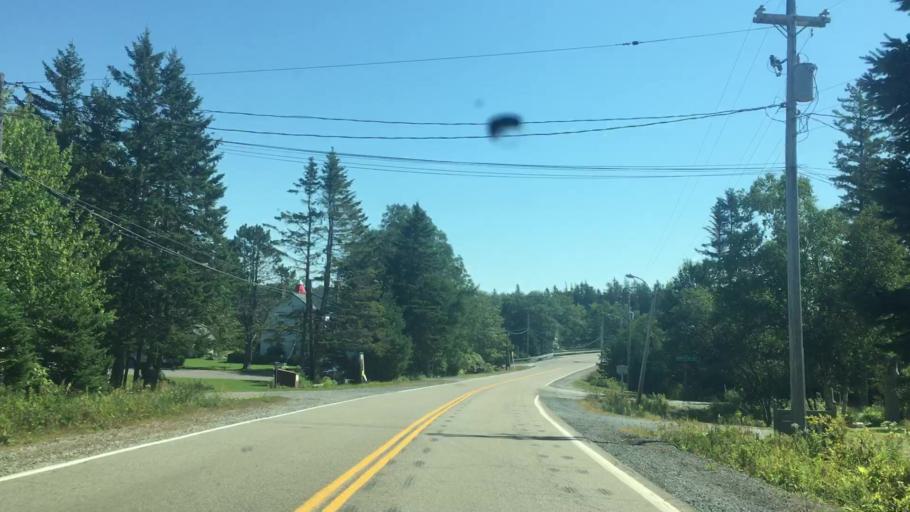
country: CA
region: Nova Scotia
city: Antigonish
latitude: 45.1442
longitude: -61.9860
